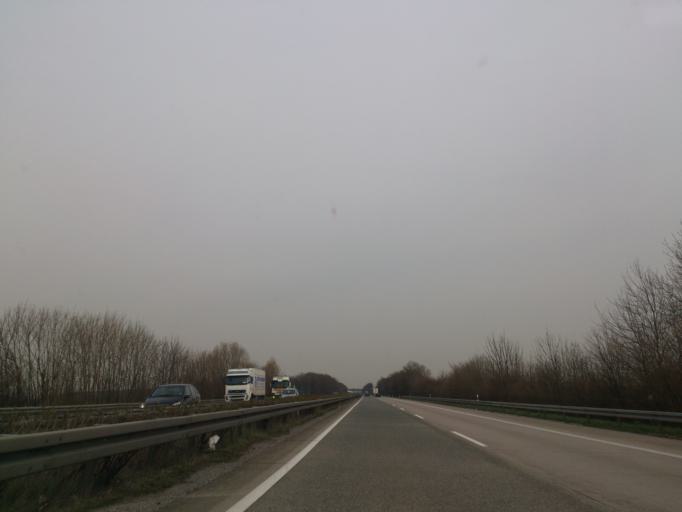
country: DE
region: North Rhine-Westphalia
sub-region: Regierungsbezirk Arnsberg
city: Anrochte
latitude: 51.5858
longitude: 8.3636
